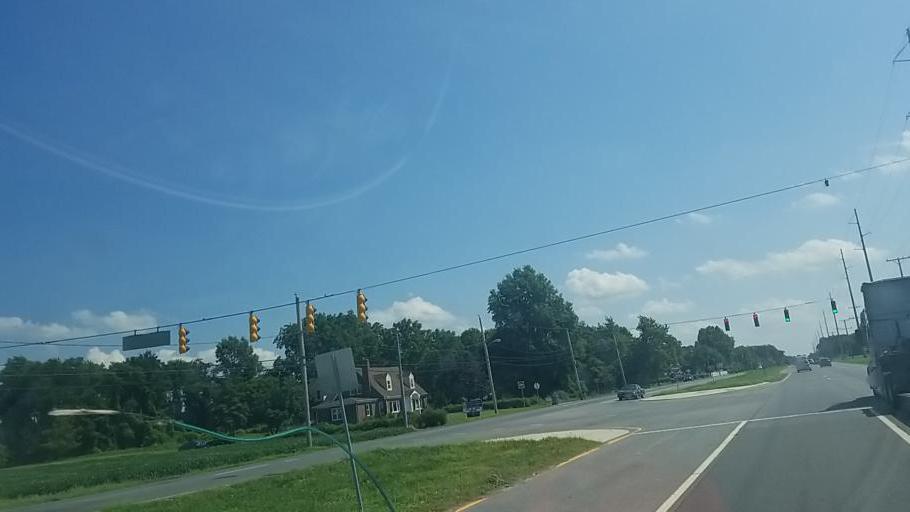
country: US
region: Delaware
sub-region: Sussex County
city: Milford
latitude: 38.8977
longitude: -75.4397
